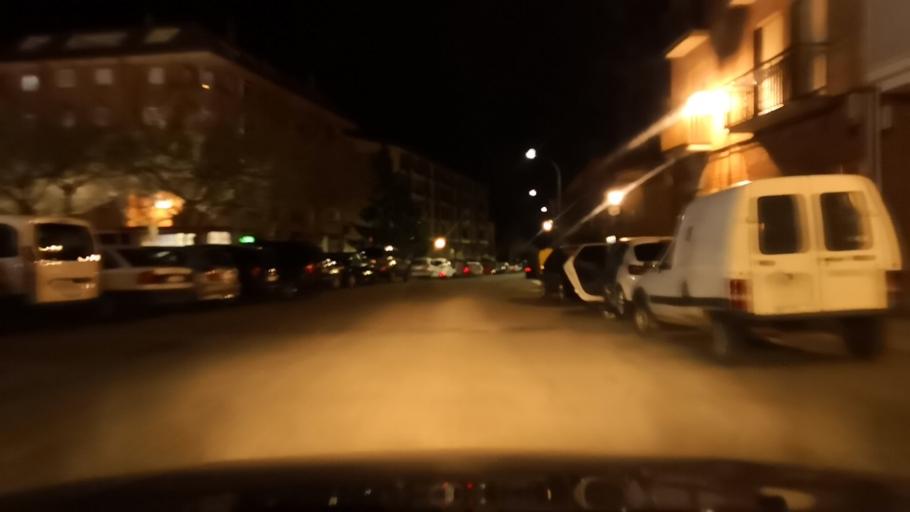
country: ES
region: Castille and Leon
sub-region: Provincia de Zamora
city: Benavente
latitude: 41.9960
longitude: -5.6797
